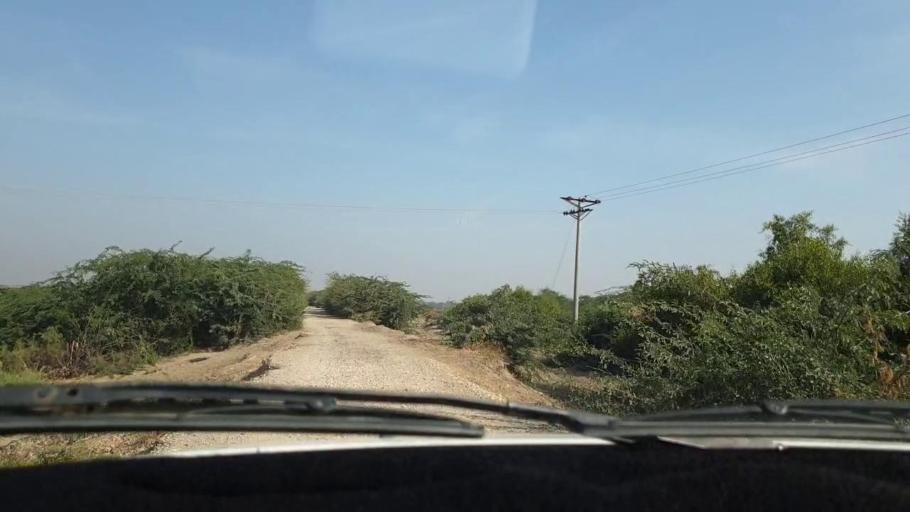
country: PK
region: Sindh
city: Tando Muhammad Khan
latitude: 24.9770
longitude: 68.4595
